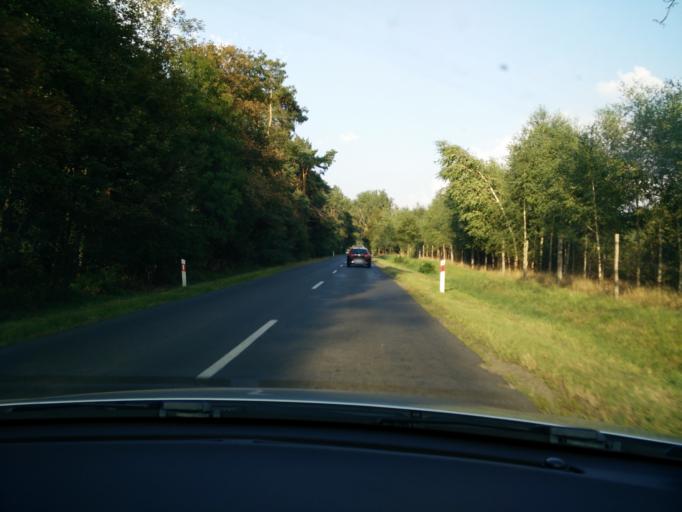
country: PL
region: Greater Poland Voivodeship
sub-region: Powiat wrzesinski
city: Miloslaw
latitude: 52.2808
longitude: 17.4813
